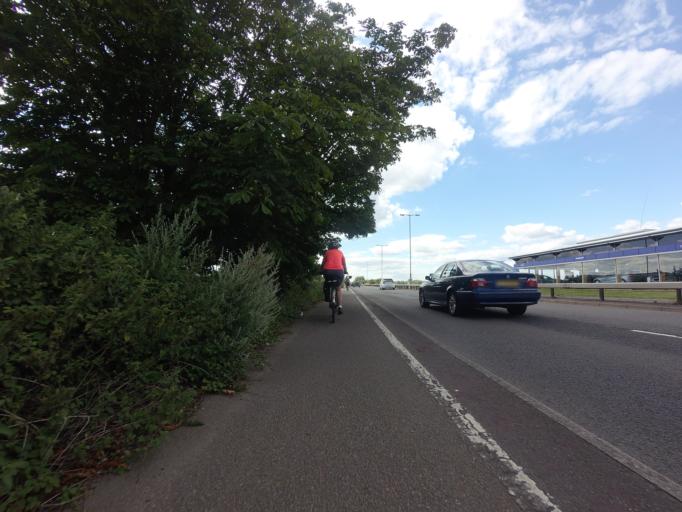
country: GB
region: England
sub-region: East Sussex
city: Eastbourne
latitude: 50.7900
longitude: 0.2977
